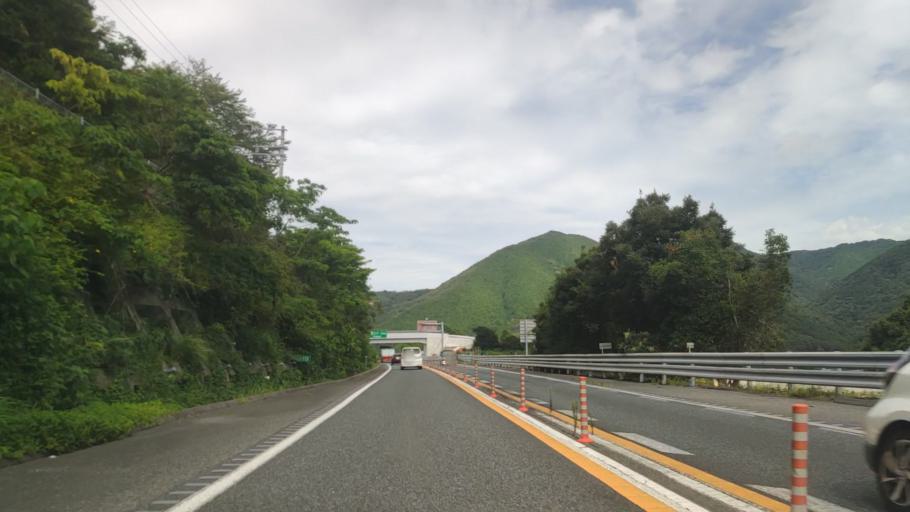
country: JP
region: Wakayama
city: Gobo
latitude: 33.9894
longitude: 135.1990
